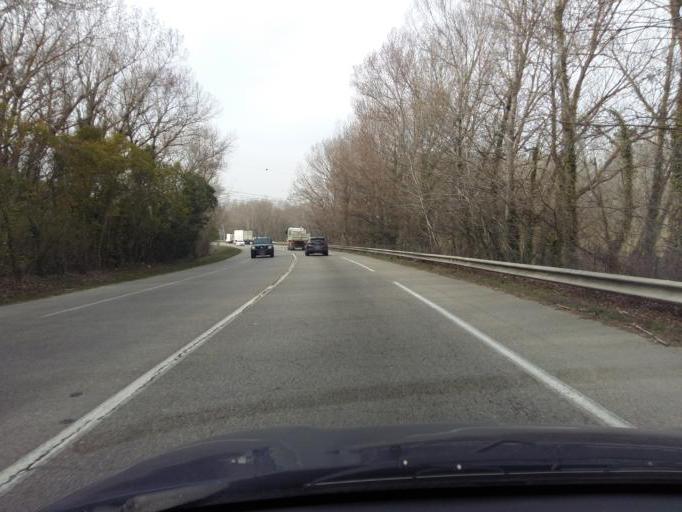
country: FR
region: Provence-Alpes-Cote d'Azur
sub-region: Departement des Bouches-du-Rhone
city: Noves
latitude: 43.8881
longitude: 4.9012
